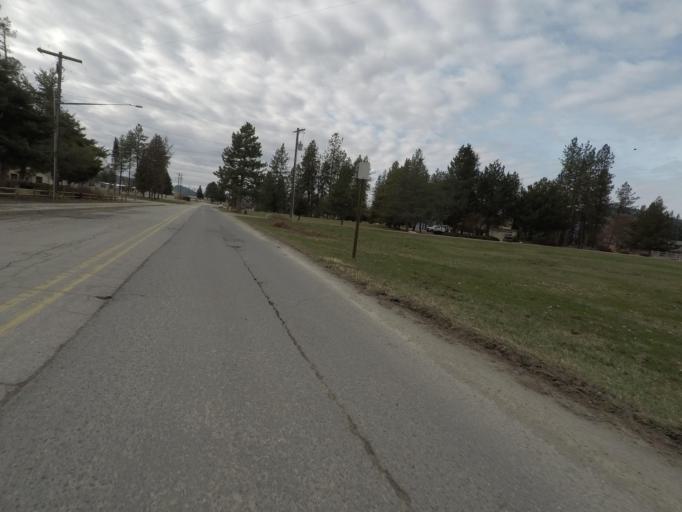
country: US
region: Washington
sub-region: Stevens County
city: Colville
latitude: 48.5452
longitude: -117.8881
